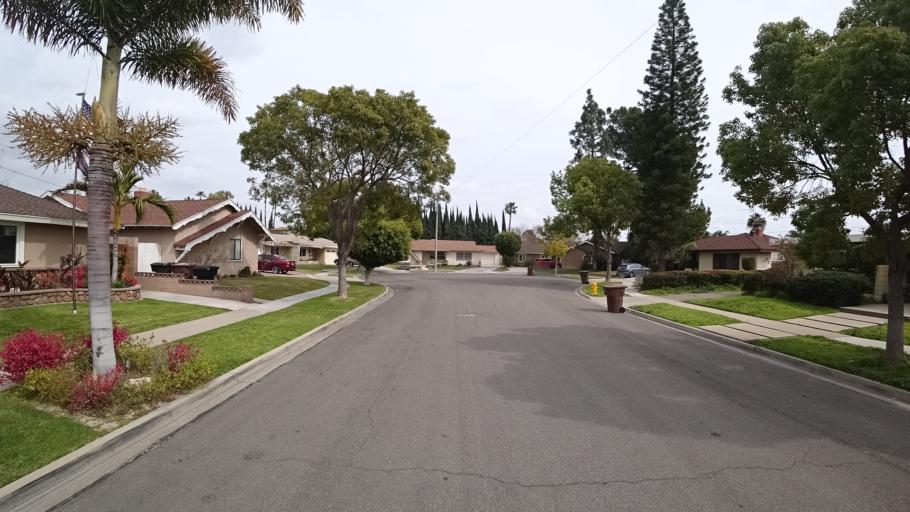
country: US
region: California
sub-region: Orange County
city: Stanton
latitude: 33.8300
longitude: -117.9791
